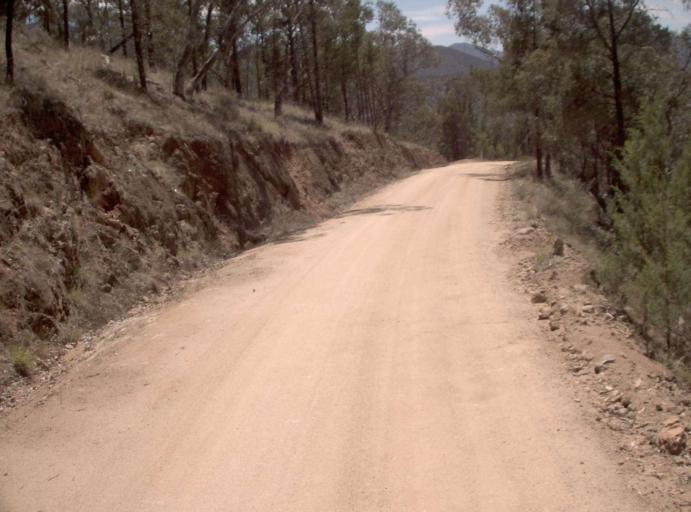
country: AU
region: New South Wales
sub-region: Snowy River
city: Jindabyne
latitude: -36.9333
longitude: 148.3646
